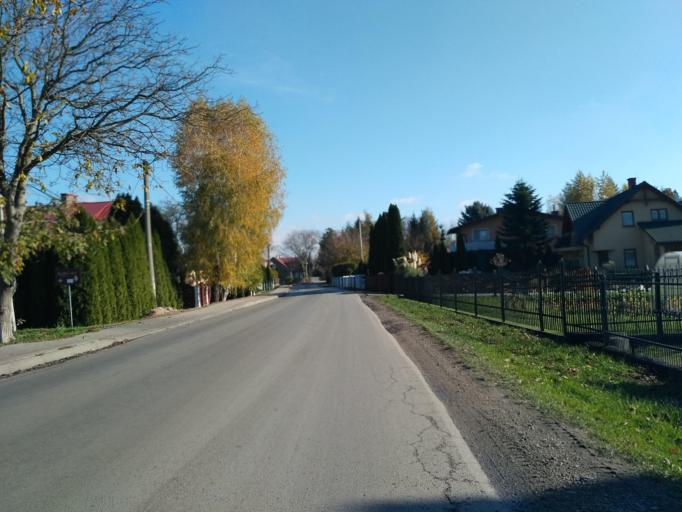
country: PL
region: Subcarpathian Voivodeship
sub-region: Powiat rzeszowski
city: Trzciana
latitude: 50.0792
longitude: 21.8358
